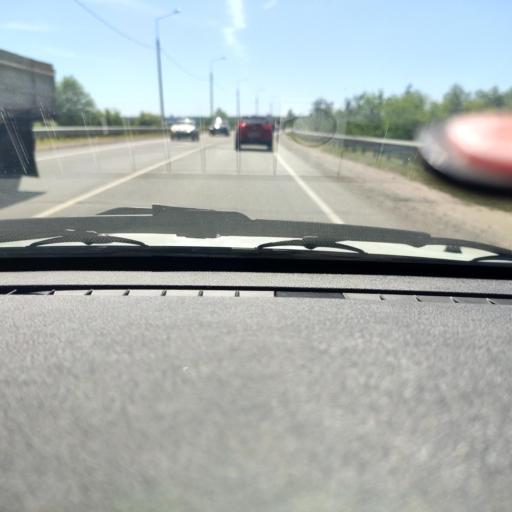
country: RU
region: Voronezj
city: Pridonskoy
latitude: 51.7212
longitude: 39.0693
